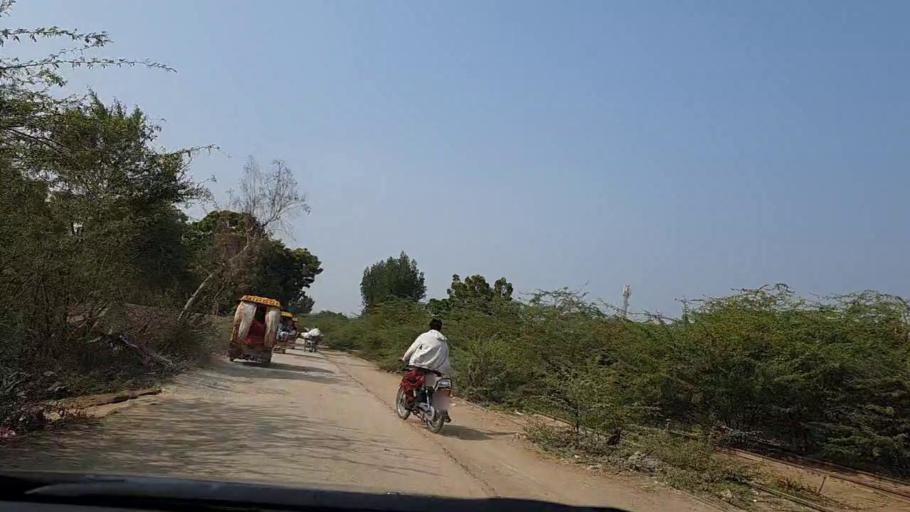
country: PK
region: Sindh
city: Sakrand
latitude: 26.1406
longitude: 68.2774
